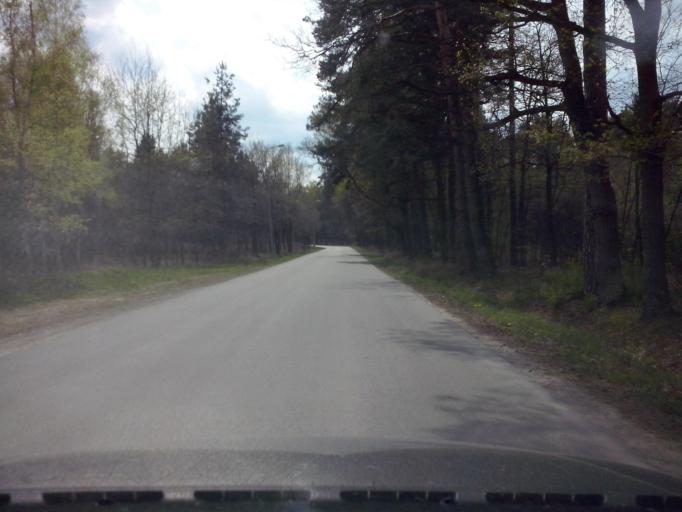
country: PL
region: Subcarpathian Voivodeship
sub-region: Powiat lezajski
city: Letownia
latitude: 50.3645
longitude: 22.2087
